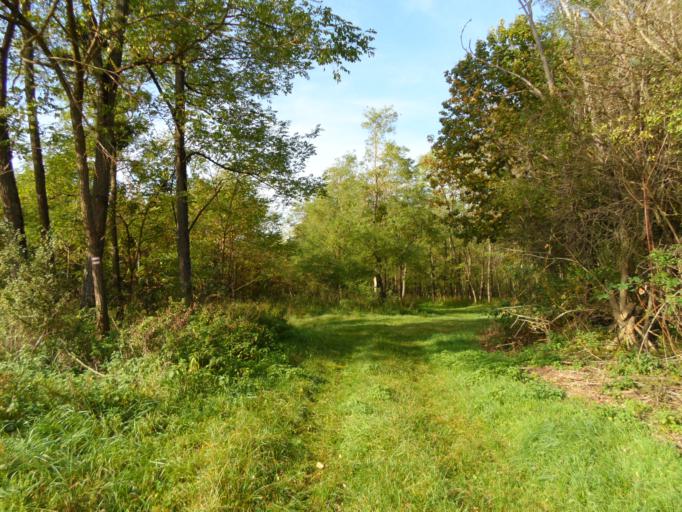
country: HU
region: Veszprem
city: Devecser
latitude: 47.2041
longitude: 17.4495
